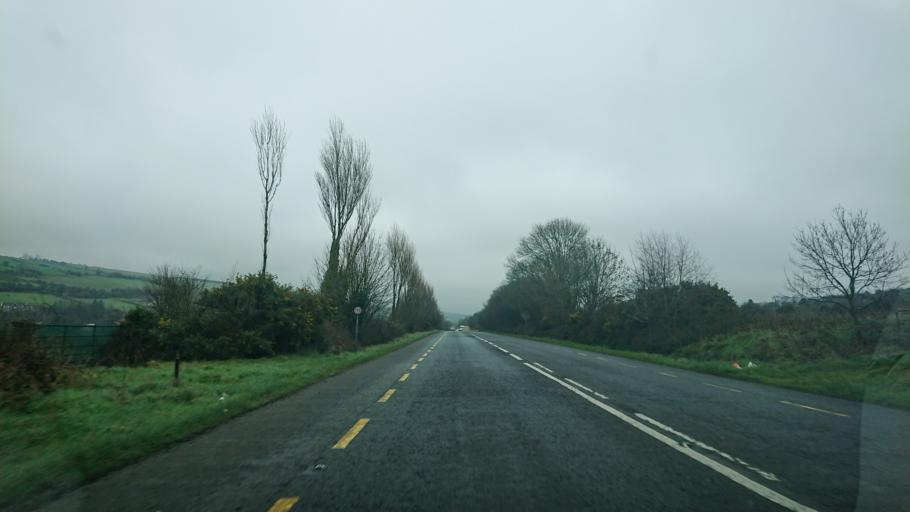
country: IE
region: Munster
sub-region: County Cork
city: Killumney
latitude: 51.7976
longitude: -8.5866
